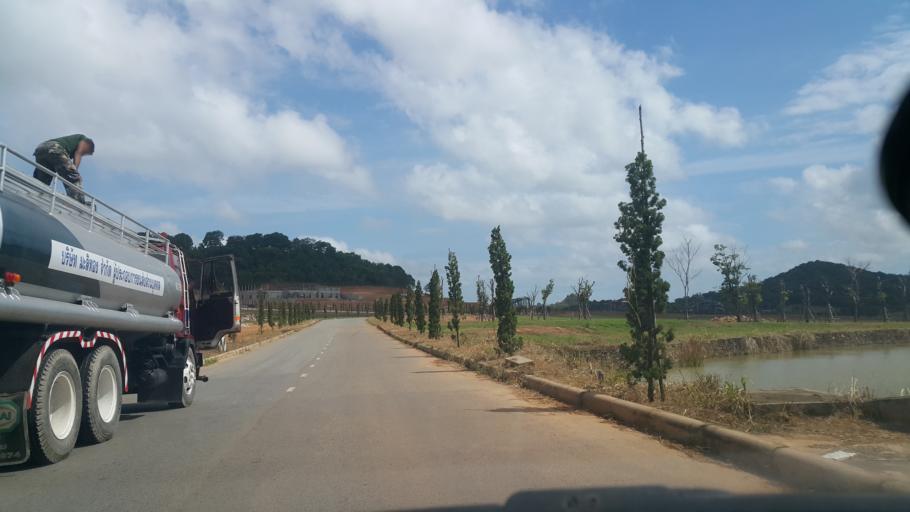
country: TH
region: Rayong
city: Ban Chang
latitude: 12.7575
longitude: 100.9663
